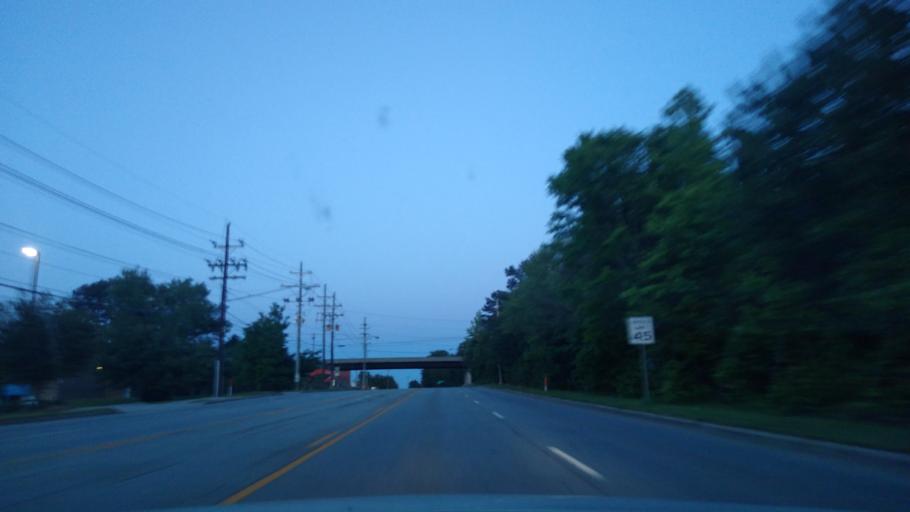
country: US
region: North Carolina
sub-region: Guilford County
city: Oak Ridge
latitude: 36.0925
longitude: -79.9560
